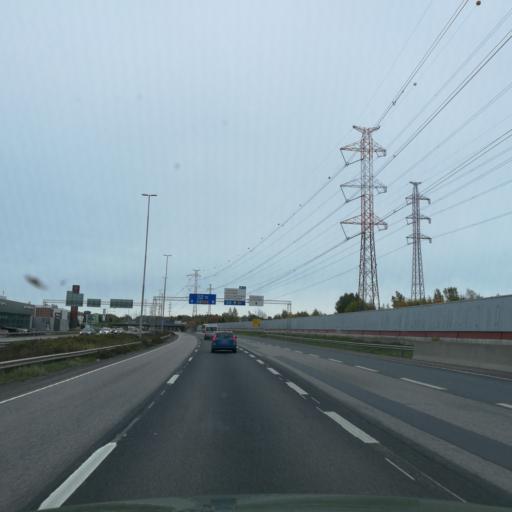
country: FI
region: Uusimaa
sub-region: Helsinki
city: Vantaa
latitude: 60.2838
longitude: 25.0204
